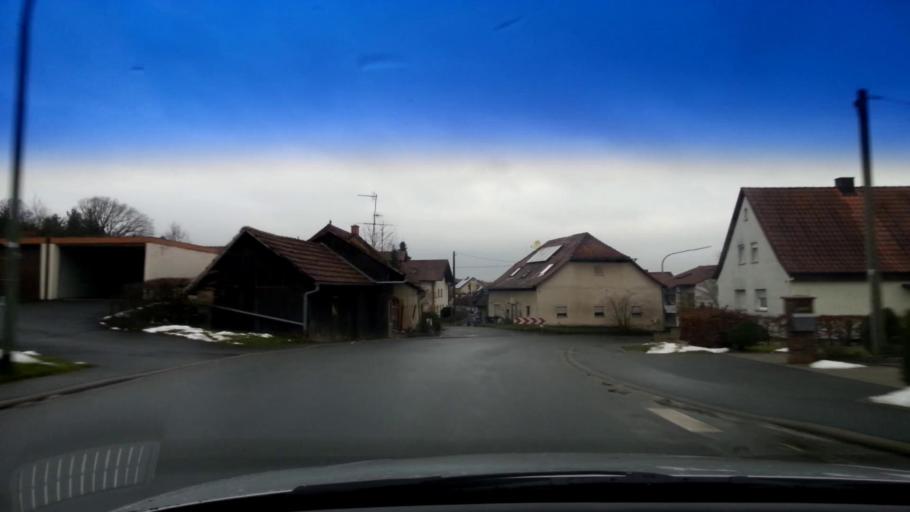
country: DE
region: Bavaria
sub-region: Upper Franconia
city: Gundelsheim
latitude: 49.9670
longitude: 10.9240
